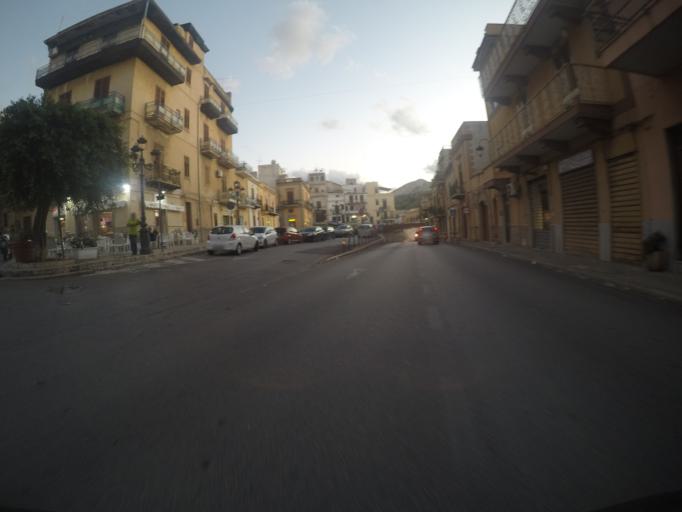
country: IT
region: Sicily
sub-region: Palermo
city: Capaci
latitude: 38.1712
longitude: 13.2394
